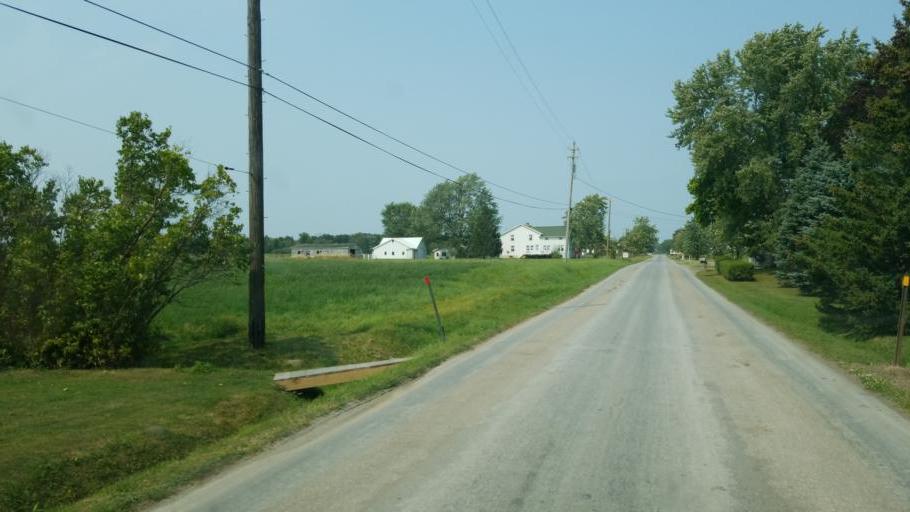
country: US
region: Ohio
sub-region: Geauga County
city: Middlefield
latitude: 41.4879
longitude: -81.0032
